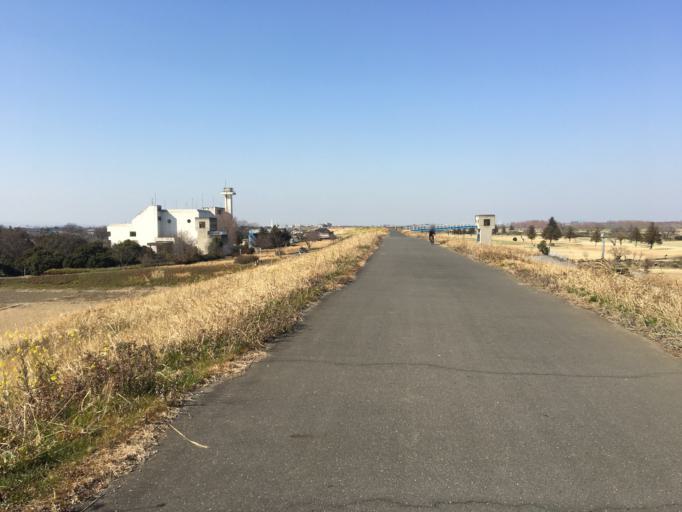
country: JP
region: Saitama
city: Shiki
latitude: 35.8700
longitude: 139.5742
